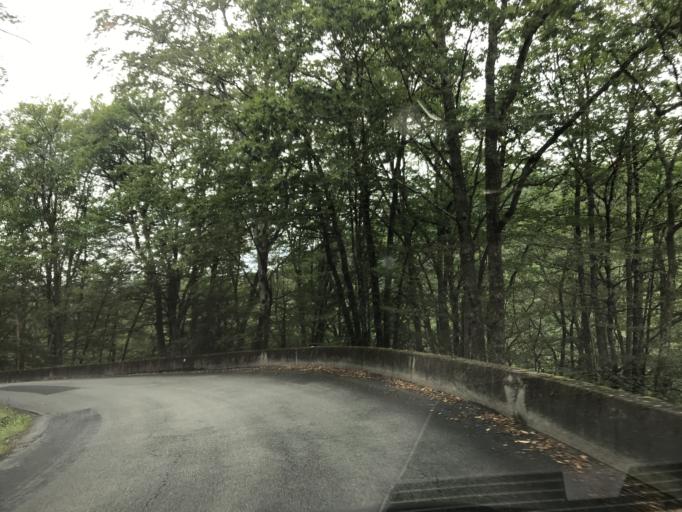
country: FR
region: Auvergne
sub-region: Departement du Cantal
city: Pleaux
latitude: 45.2370
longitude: 2.1772
